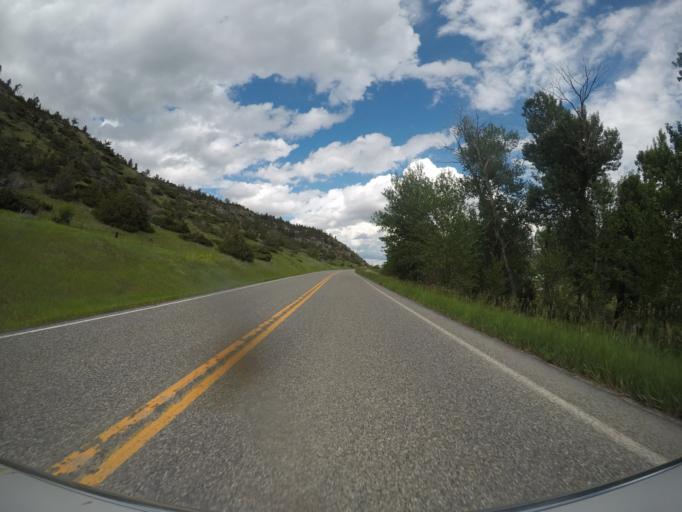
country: US
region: Montana
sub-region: Sweet Grass County
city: Big Timber
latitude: 45.6690
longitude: -110.1048
